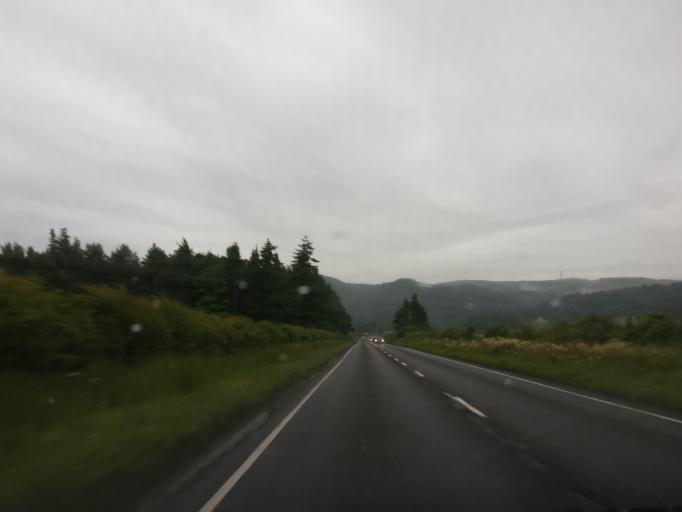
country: GB
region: Scotland
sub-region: Perth and Kinross
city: Bridge of Earn
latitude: 56.3322
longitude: -3.3707
